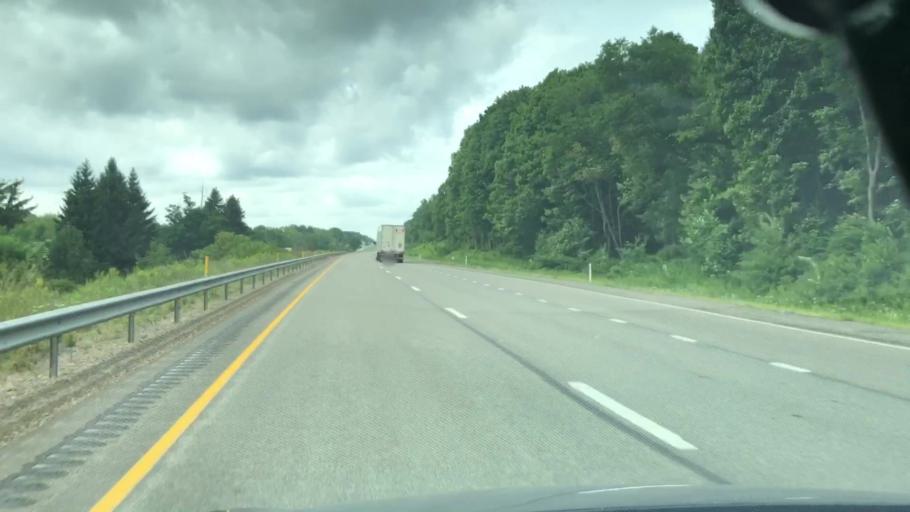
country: US
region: Pennsylvania
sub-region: Crawford County
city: Meadville
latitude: 41.6271
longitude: -80.1861
